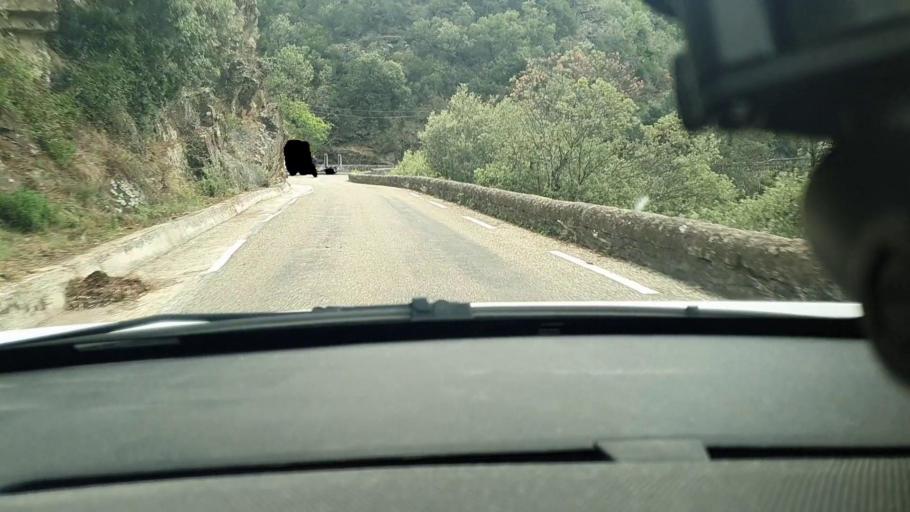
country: FR
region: Languedoc-Roussillon
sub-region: Departement du Gard
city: Besseges
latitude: 44.2997
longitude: 4.0362
